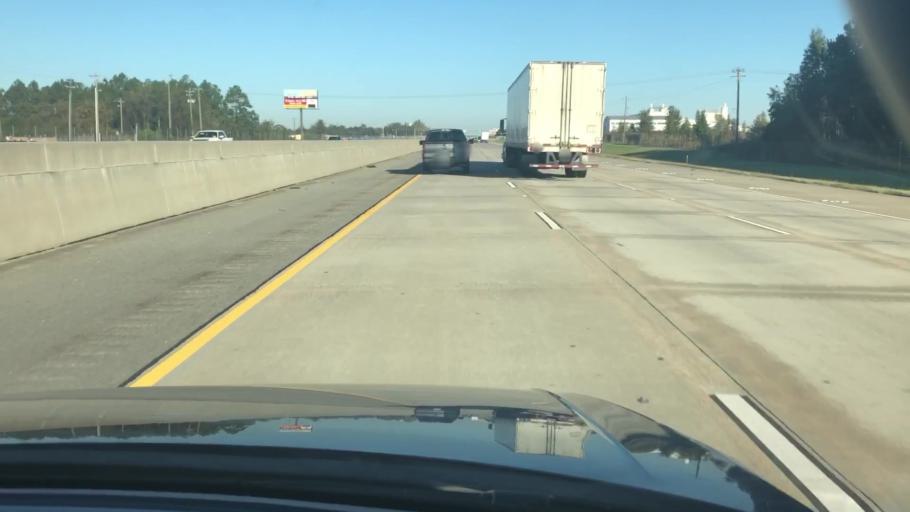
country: US
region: Georgia
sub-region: Cook County
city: Adel
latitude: 31.1040
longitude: -83.4232
